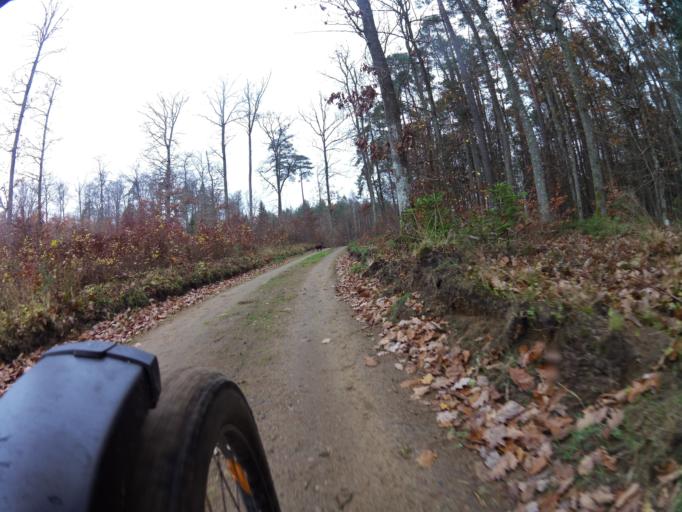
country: PL
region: Pomeranian Voivodeship
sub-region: Powiat wejherowski
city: Orle
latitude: 54.6970
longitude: 18.1566
